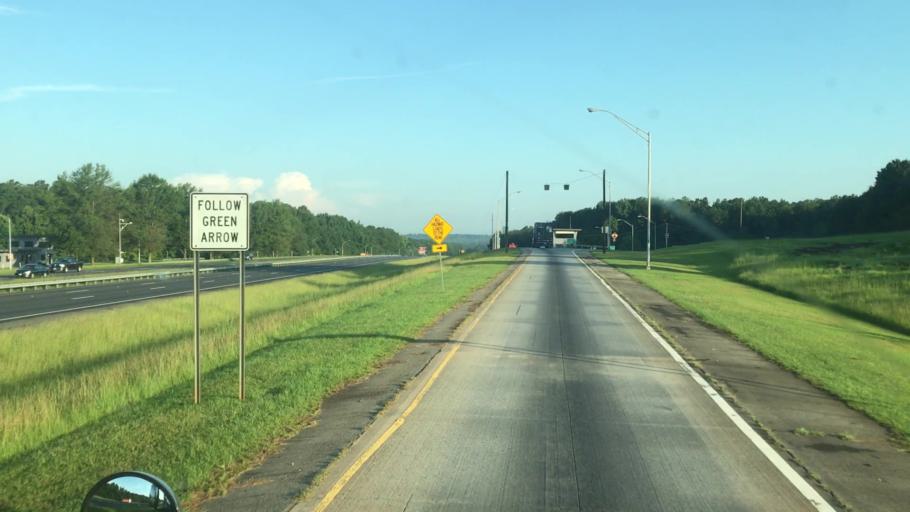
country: US
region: Georgia
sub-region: Monroe County
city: Forsyth
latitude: 33.0688
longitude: -83.9714
